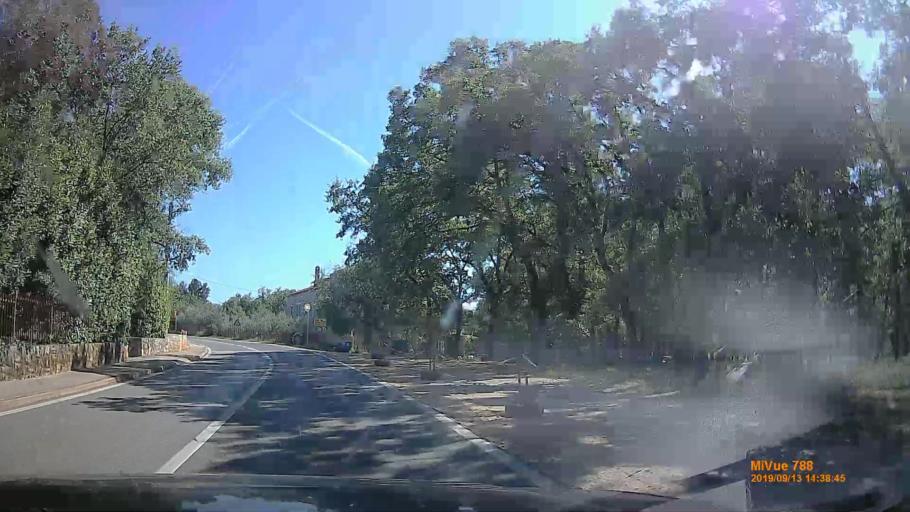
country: HR
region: Istarska
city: Umag
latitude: 45.3993
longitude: 13.5385
